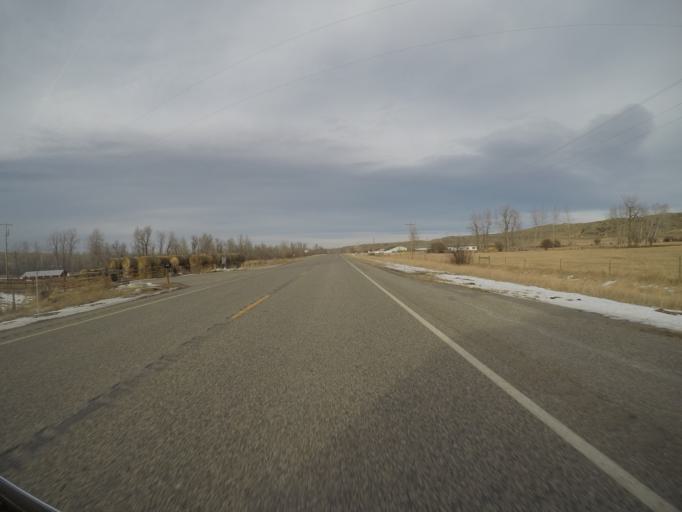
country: US
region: Montana
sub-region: Stillwater County
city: Absarokee
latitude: 45.4557
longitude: -109.4489
